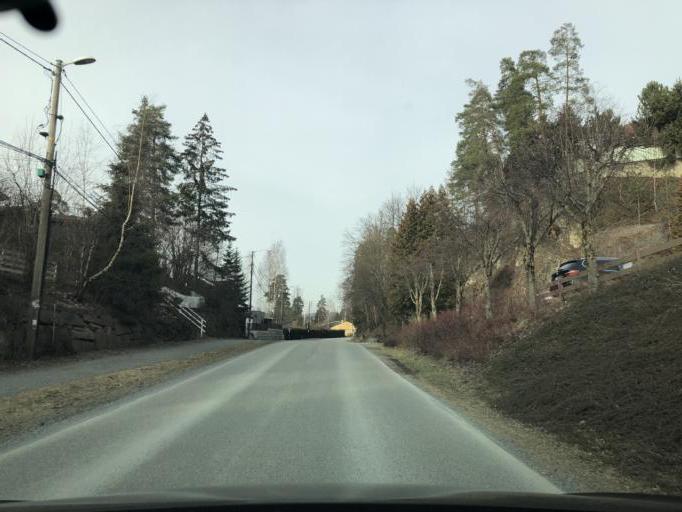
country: NO
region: Akershus
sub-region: Baerum
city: Sandvika
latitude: 59.8668
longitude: 10.5144
